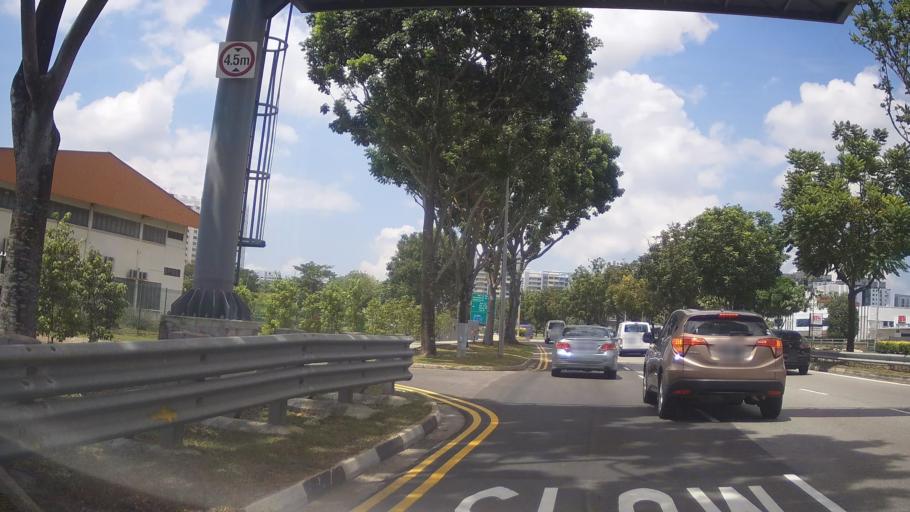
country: MY
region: Johor
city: Johor Bahru
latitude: 1.3374
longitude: 103.7096
